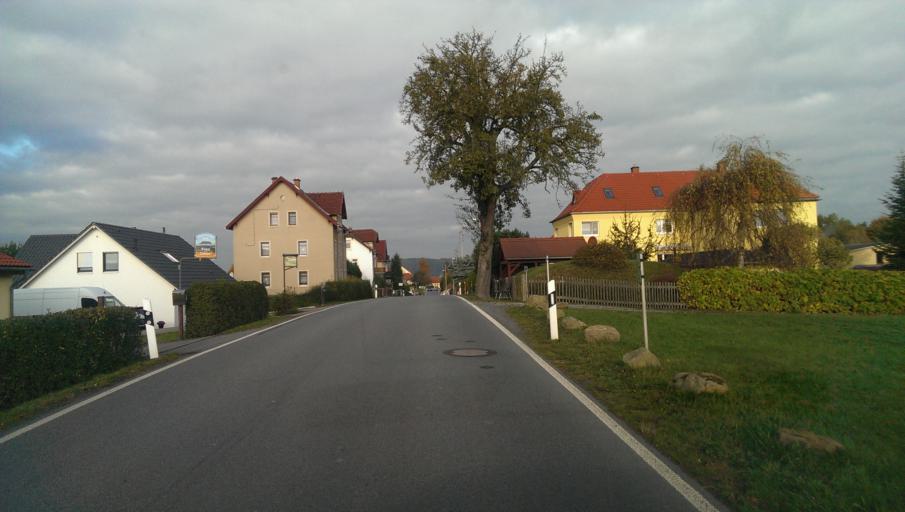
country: DE
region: Saxony
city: Porschdorf
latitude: 50.9498
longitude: 14.1119
